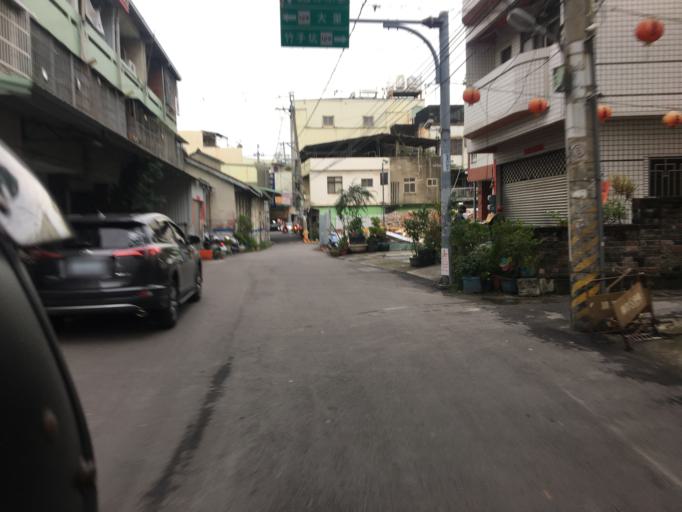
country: TW
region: Taiwan
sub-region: Taichung City
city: Taichung
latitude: 24.0952
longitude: 120.7015
